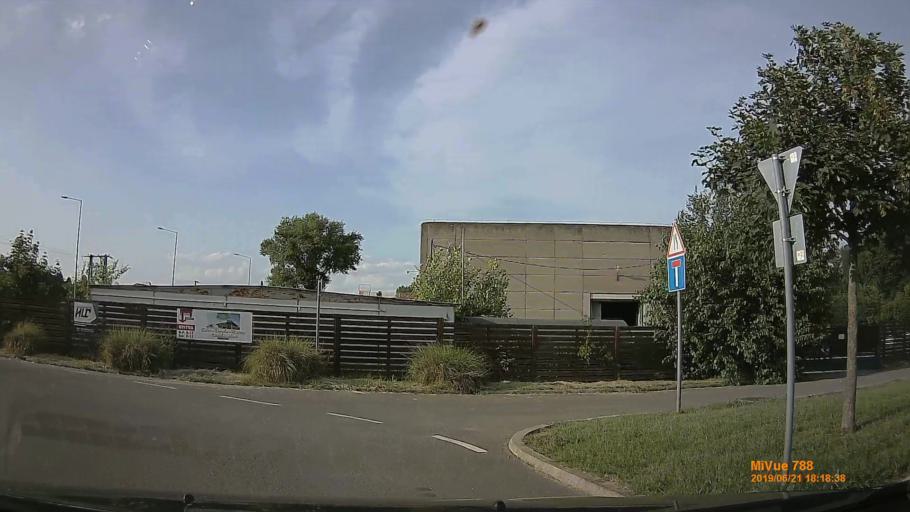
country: HU
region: Tolna
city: Paks
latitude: 46.6101
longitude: 18.8516
